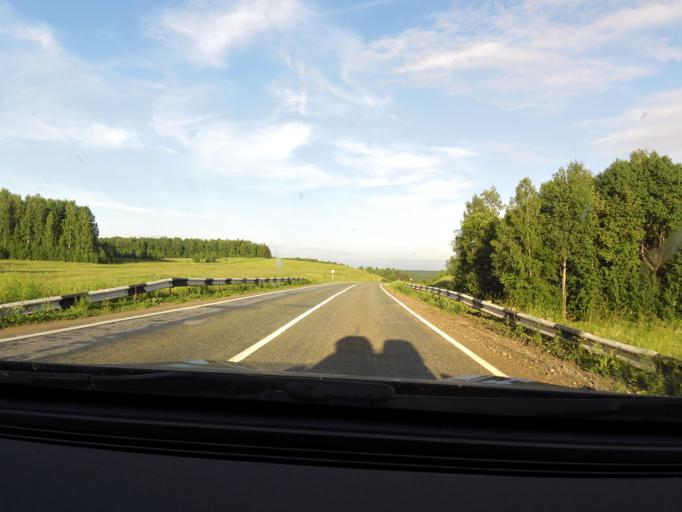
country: RU
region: Perm
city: Siva
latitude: 58.6407
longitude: 53.8399
